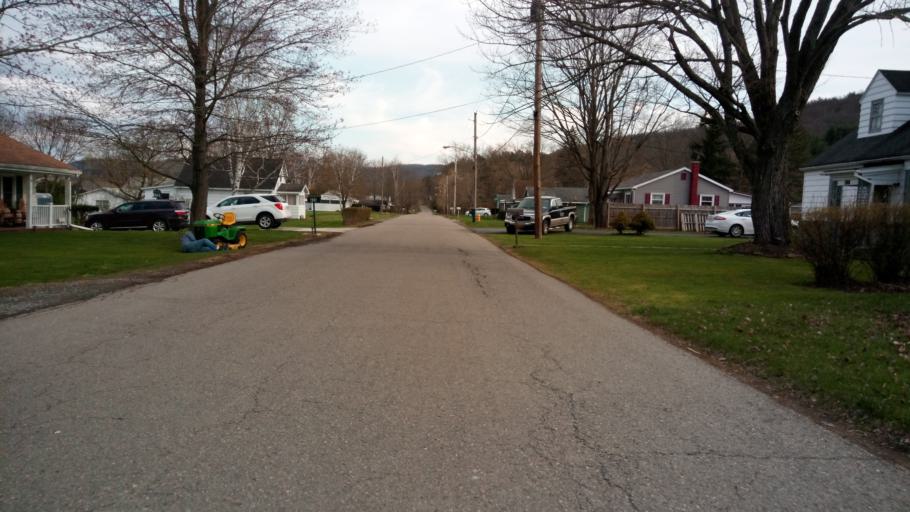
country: US
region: New York
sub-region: Chemung County
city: Southport
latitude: 42.0731
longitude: -76.8243
